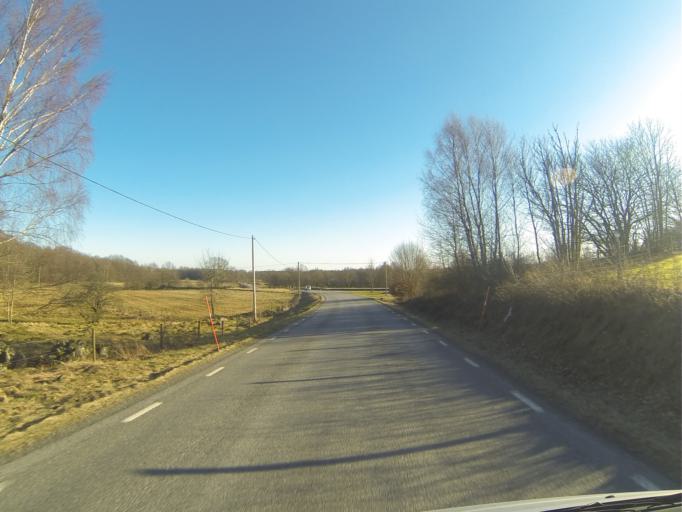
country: SE
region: Skane
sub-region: Horby Kommun
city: Hoerby
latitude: 55.8972
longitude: 13.6623
